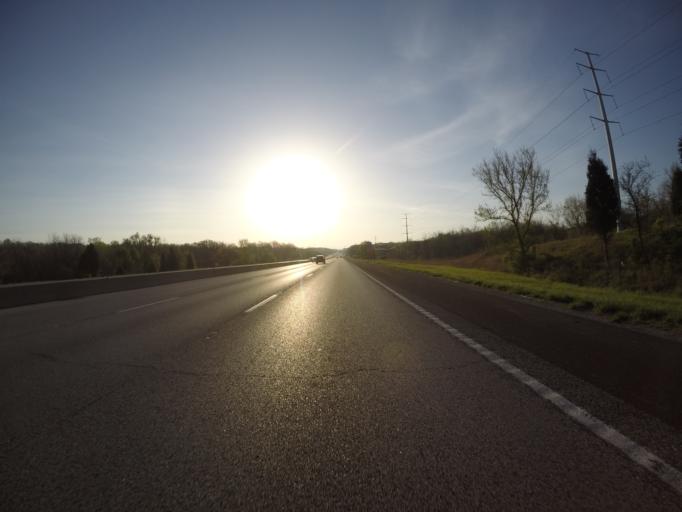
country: US
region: Missouri
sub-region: Jackson County
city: Raytown
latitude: 38.9370
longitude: -94.4612
